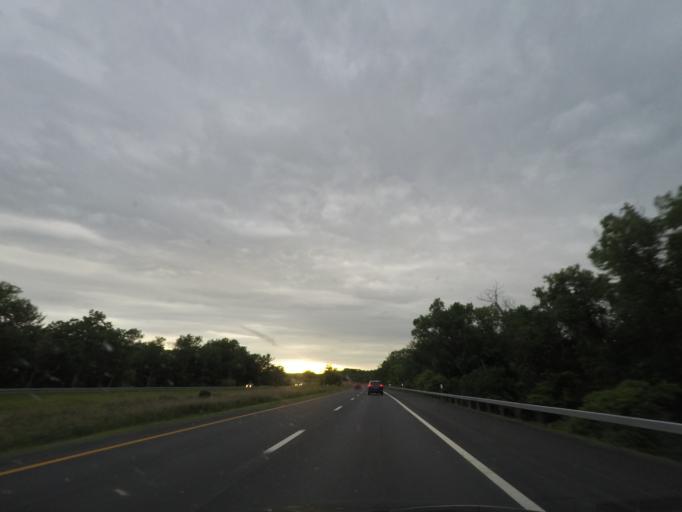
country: US
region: New York
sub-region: Rensselaer County
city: Nassau
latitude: 42.4810
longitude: -73.6258
